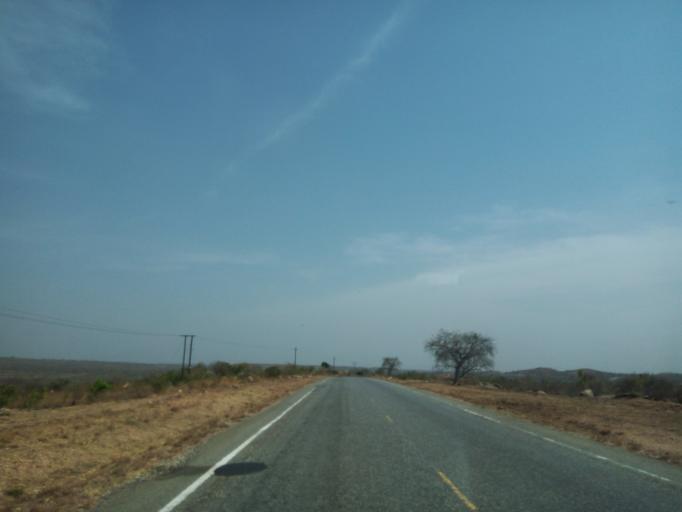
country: UG
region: Northern Region
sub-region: Nebbi District
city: Nebbi
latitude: 2.4428
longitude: 31.2530
